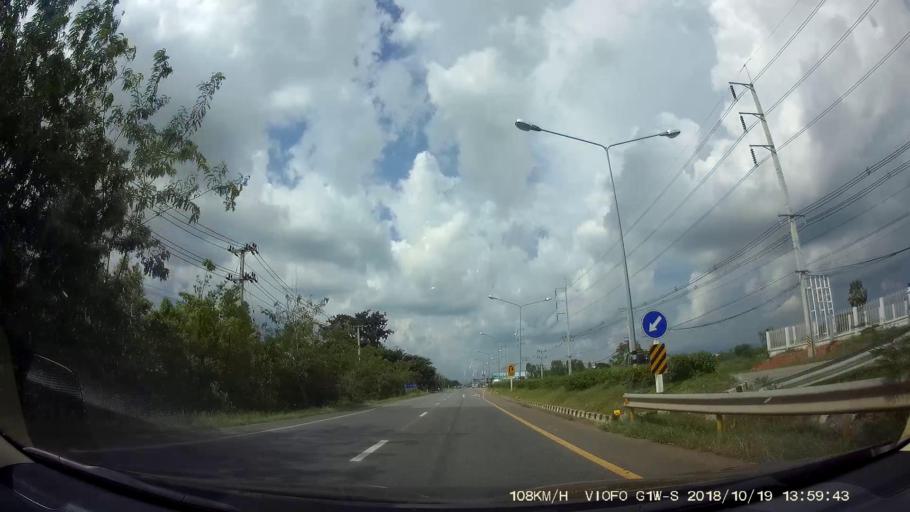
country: TH
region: Chaiyaphum
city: Chaiyaphum
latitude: 15.8137
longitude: 102.0604
